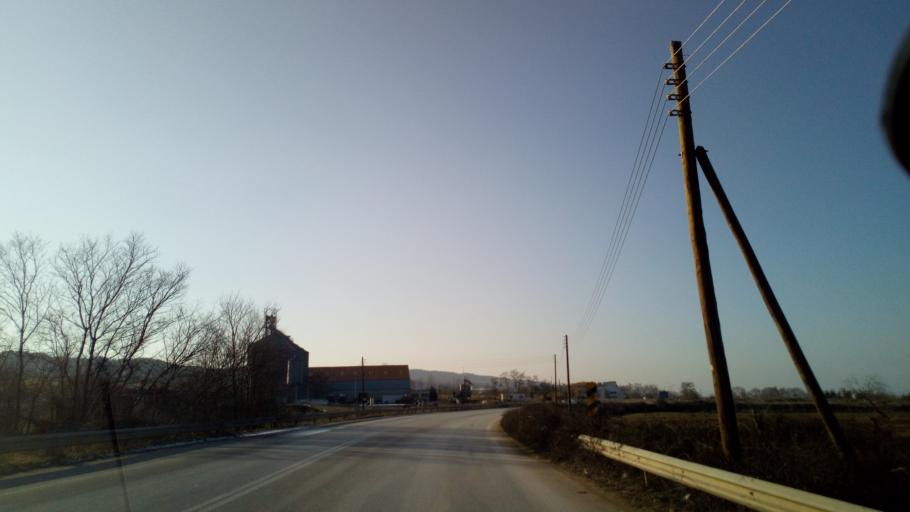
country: GR
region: Central Macedonia
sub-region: Nomos Thessalonikis
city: Gerakarou
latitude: 40.6318
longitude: 23.2023
